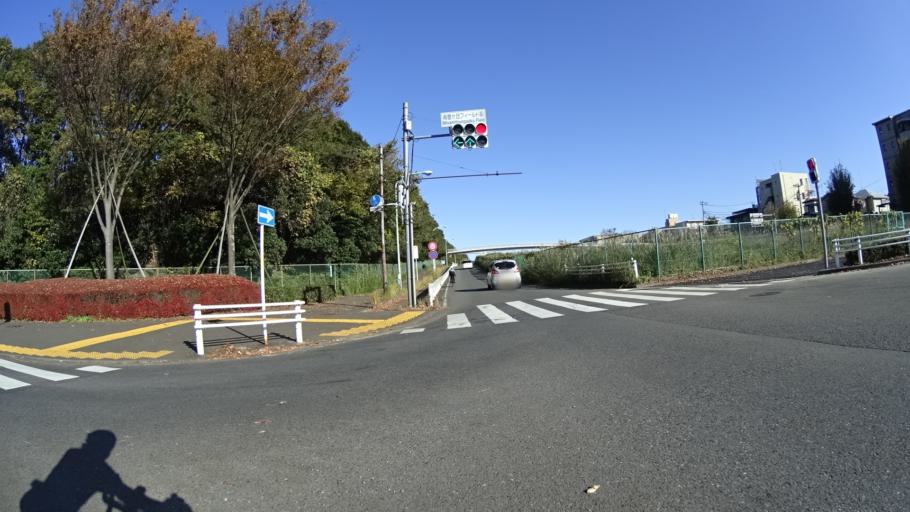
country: JP
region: Tokyo
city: Hino
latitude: 35.6102
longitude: 139.4325
